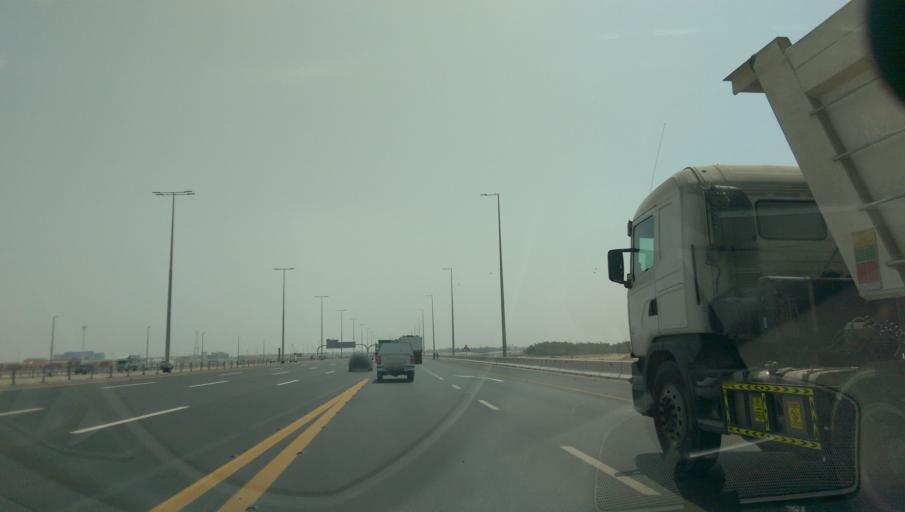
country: AE
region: Abu Dhabi
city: Abu Dhabi
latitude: 24.2990
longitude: 54.5860
